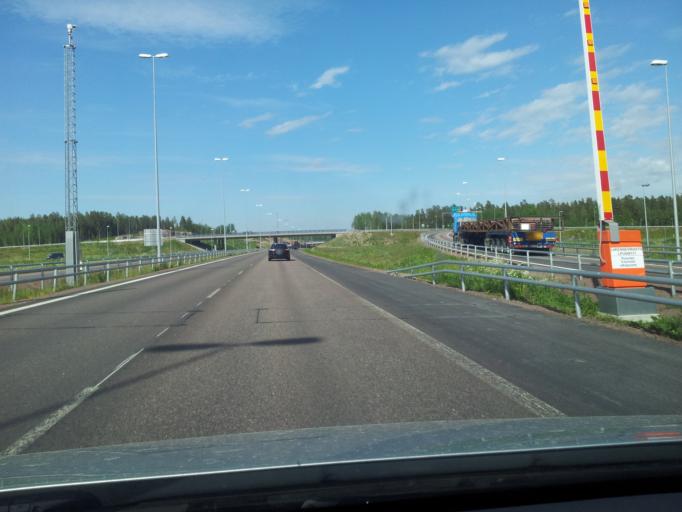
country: FI
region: Kymenlaakso
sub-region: Kotka-Hamina
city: Hamina
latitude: 60.5847
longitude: 27.1505
